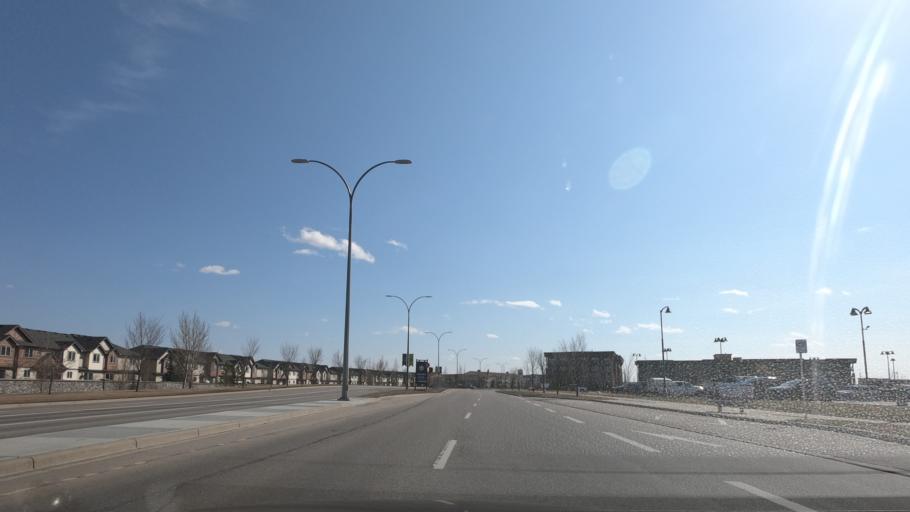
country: CA
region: Alberta
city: Airdrie
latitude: 51.2702
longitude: -113.9900
